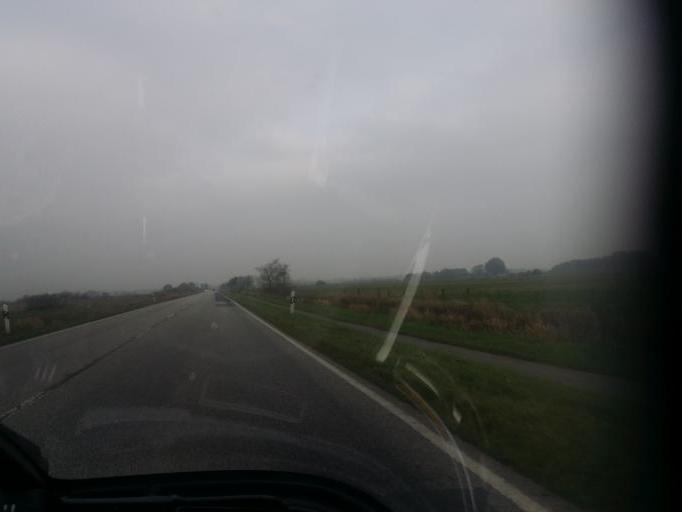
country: DE
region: Schleswig-Holstein
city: Hattstedtermarsch
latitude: 54.5595
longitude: 9.0004
